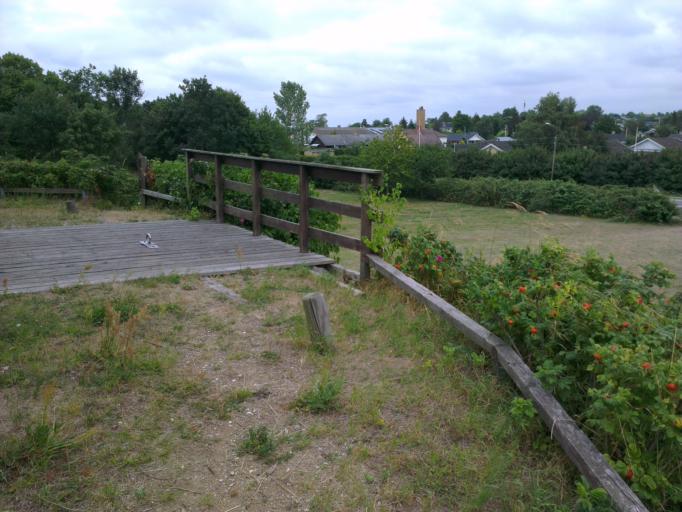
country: DK
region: Capital Region
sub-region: Frederikssund Kommune
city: Jaegerspris
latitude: 55.8483
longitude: 11.9871
